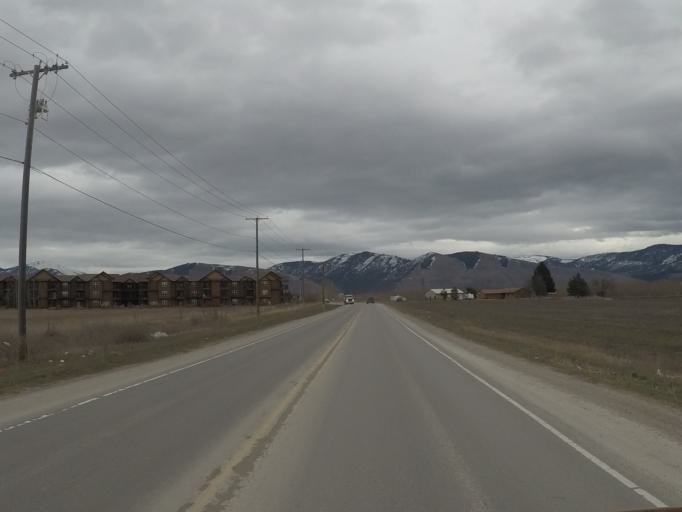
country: US
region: Montana
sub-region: Missoula County
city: Orchard Homes
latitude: 46.8868
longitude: -114.0528
